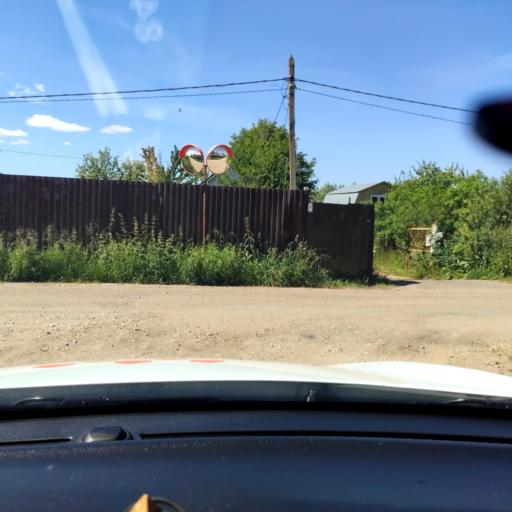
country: RU
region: Tatarstan
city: Vysokaya Gora
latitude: 55.8166
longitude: 49.2867
